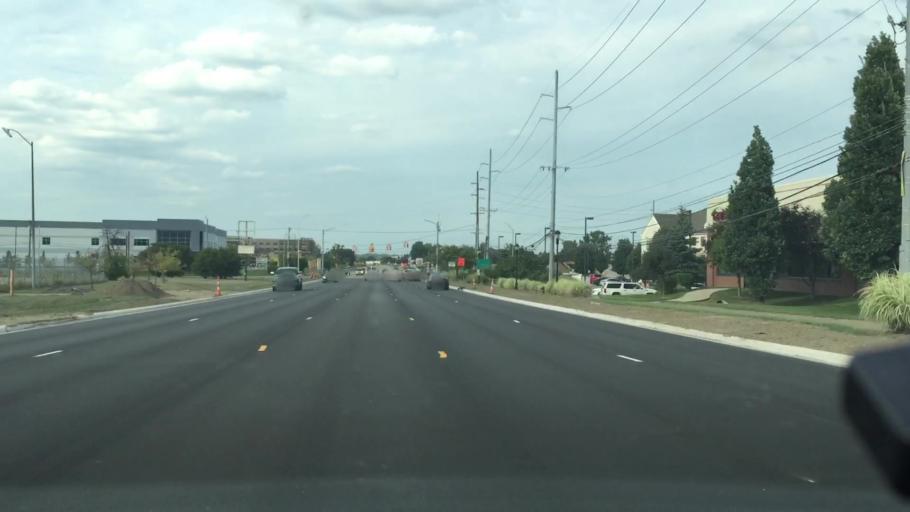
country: US
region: Michigan
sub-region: Oakland County
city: Auburn Hills
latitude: 42.6474
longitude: -83.2489
